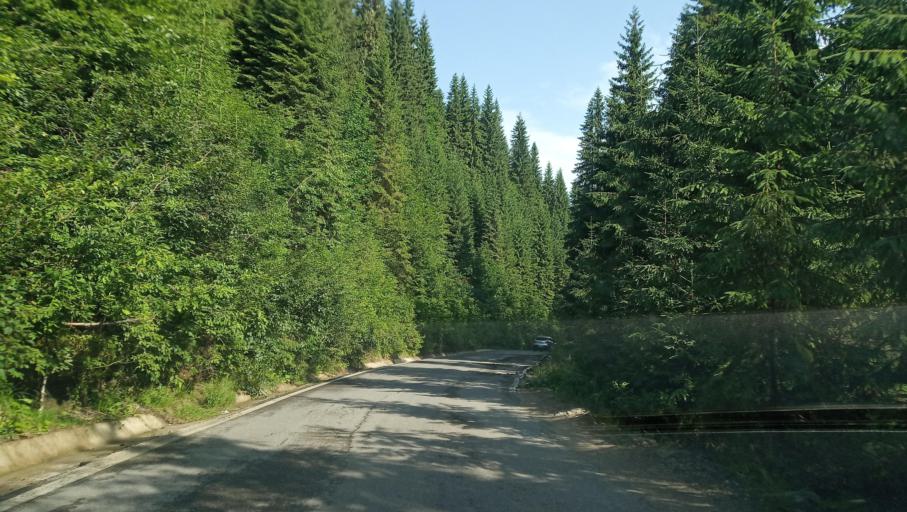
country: RO
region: Dambovita
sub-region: Comuna Moroeni
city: Glod
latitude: 45.3264
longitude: 25.4342
